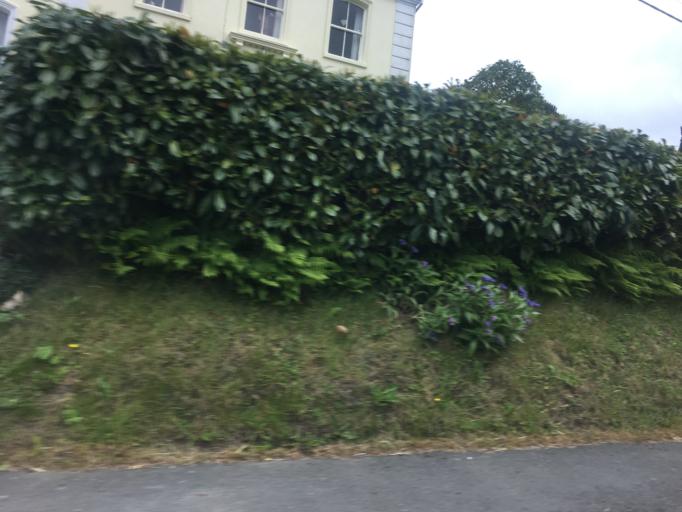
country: GB
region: Wales
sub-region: Carmarthenshire
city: Llansawel
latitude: 52.0484
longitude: -3.9618
